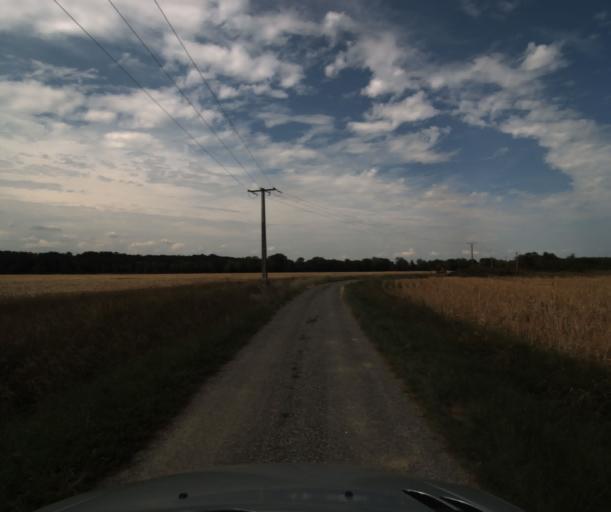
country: FR
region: Midi-Pyrenees
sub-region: Departement de la Haute-Garonne
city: Labastidette
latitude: 43.4880
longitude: 1.2176
